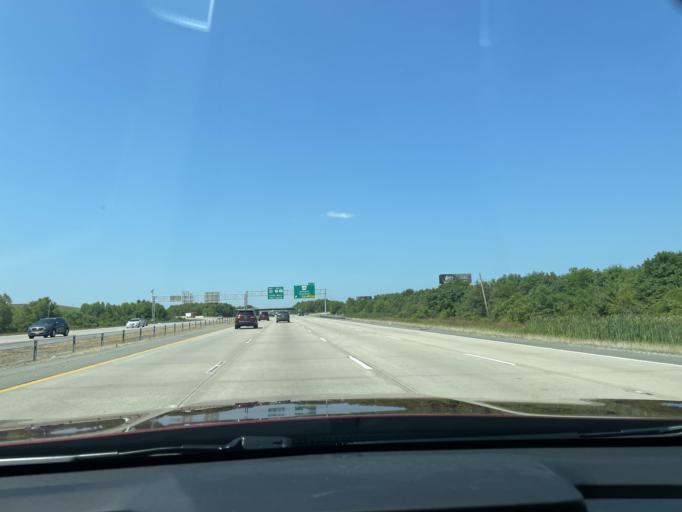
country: US
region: Arkansas
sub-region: Pulaski County
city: Jacksonville
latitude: 34.8482
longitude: -92.1474
